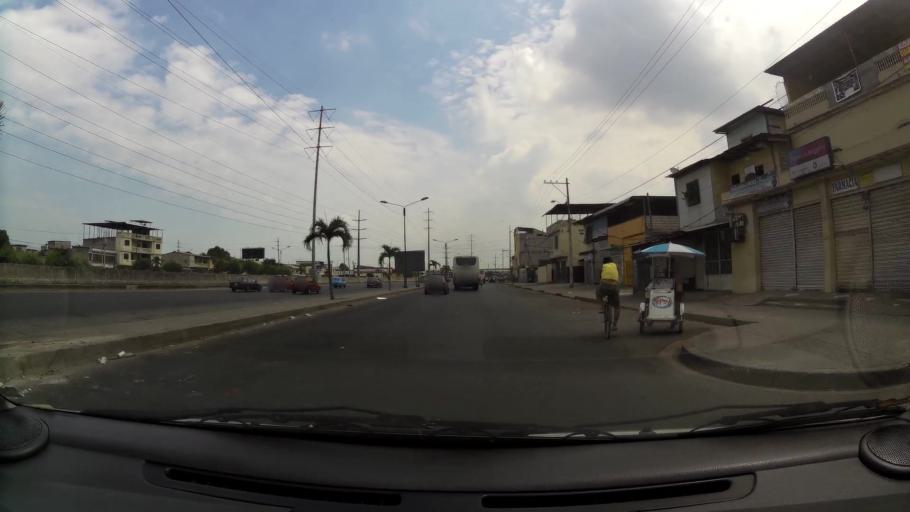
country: EC
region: Guayas
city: Guayaquil
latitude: -2.2395
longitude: -79.9168
